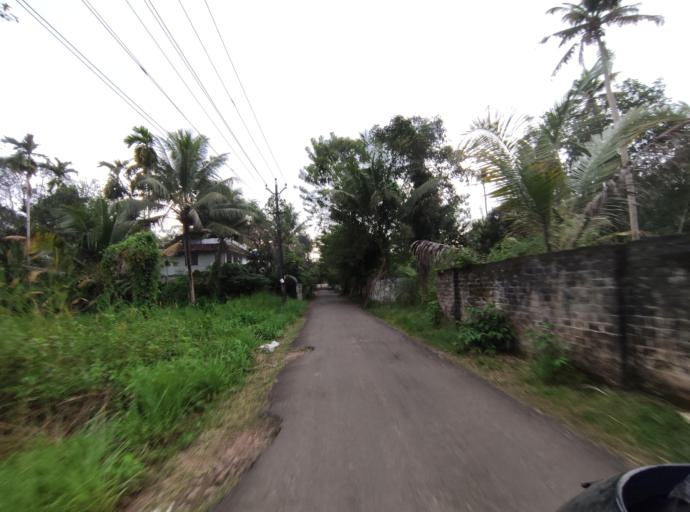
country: IN
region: Kerala
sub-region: Alappuzha
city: Shertallai
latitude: 9.6704
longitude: 76.3451
